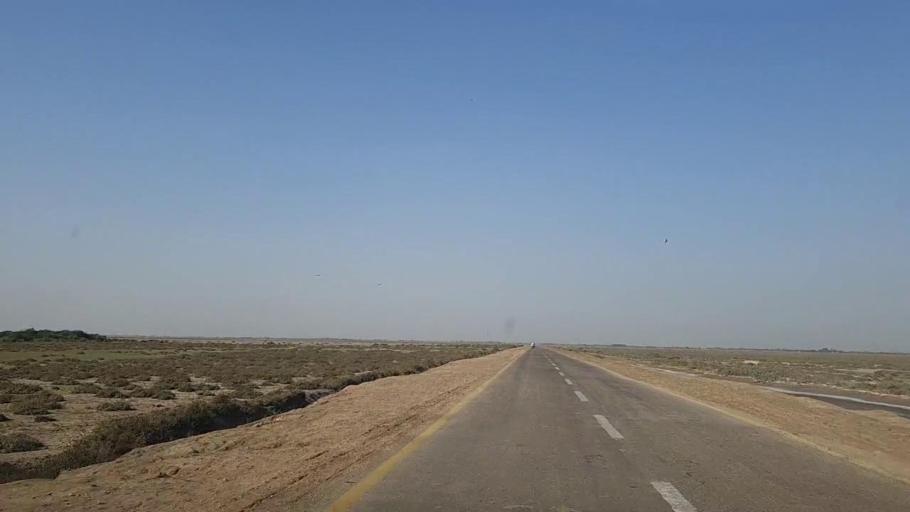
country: PK
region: Sindh
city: Jati
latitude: 24.4865
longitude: 68.3744
